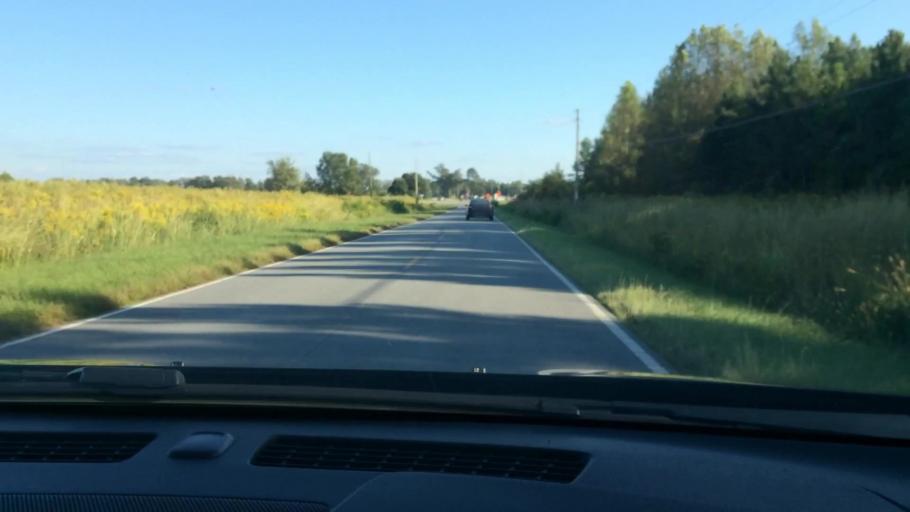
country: US
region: North Carolina
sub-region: Pitt County
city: Ayden
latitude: 35.4937
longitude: -77.4307
